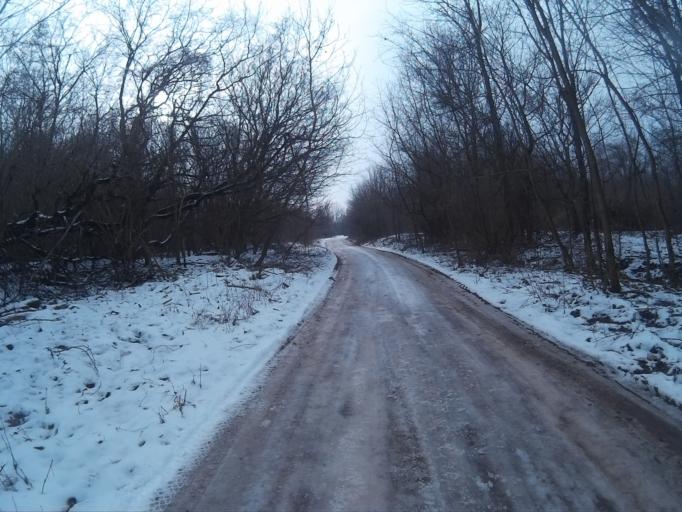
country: HU
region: Komarom-Esztergom
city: Labatlan
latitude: 47.6878
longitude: 18.5168
